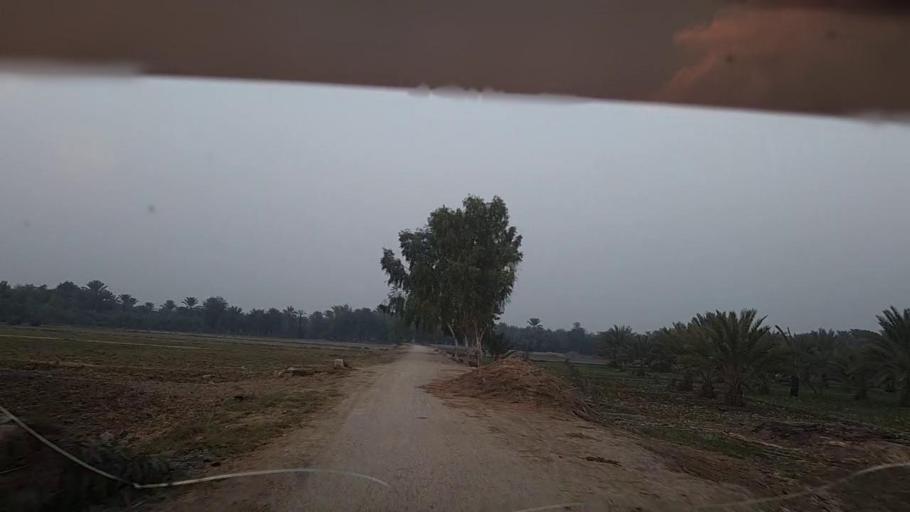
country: PK
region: Sindh
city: Khairpur
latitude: 27.5785
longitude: 68.7359
